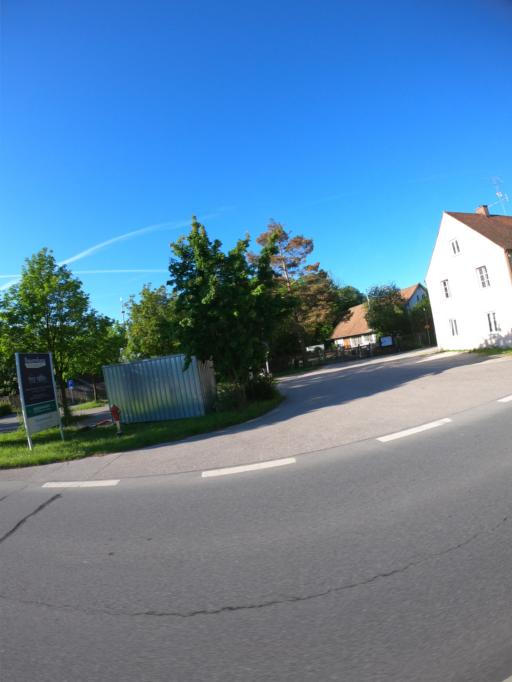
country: DE
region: Bavaria
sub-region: Upper Bavaria
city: Erding
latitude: 48.3045
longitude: 11.9245
